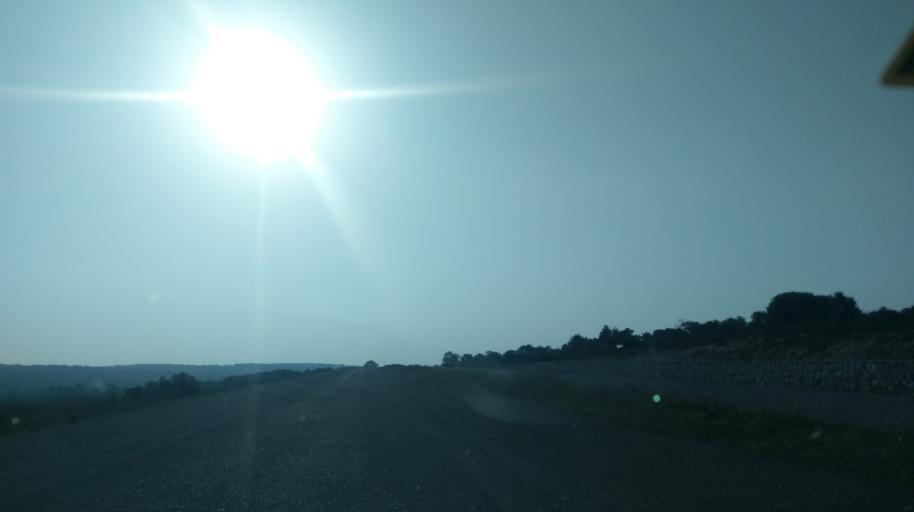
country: CY
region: Ammochostos
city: Leonarisso
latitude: 35.5147
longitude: 34.1569
